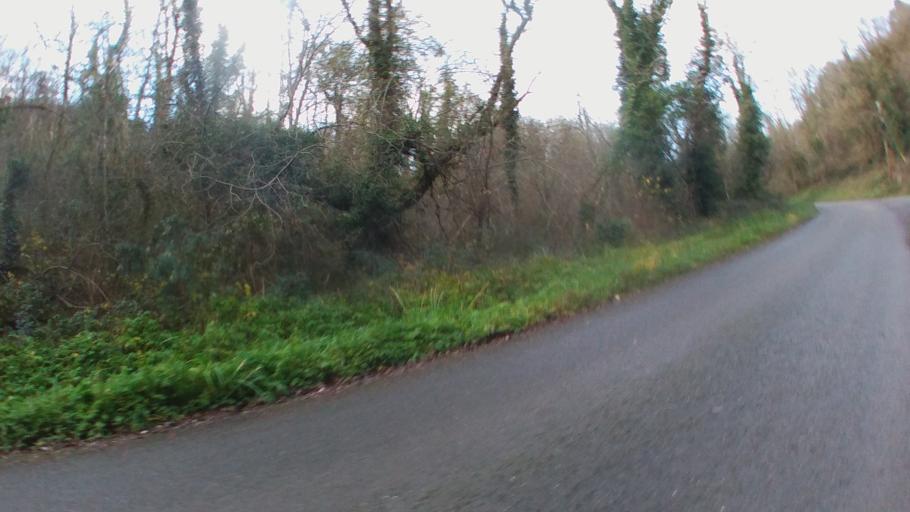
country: IE
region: Leinster
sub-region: Kilkenny
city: Kilkenny
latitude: 52.6958
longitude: -7.1683
